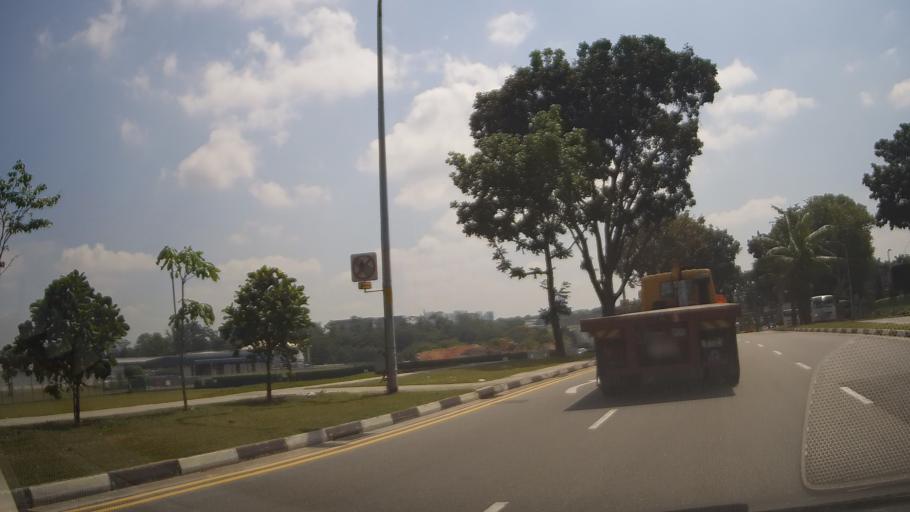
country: MY
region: Johor
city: Johor Bahru
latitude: 1.4238
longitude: 103.7578
